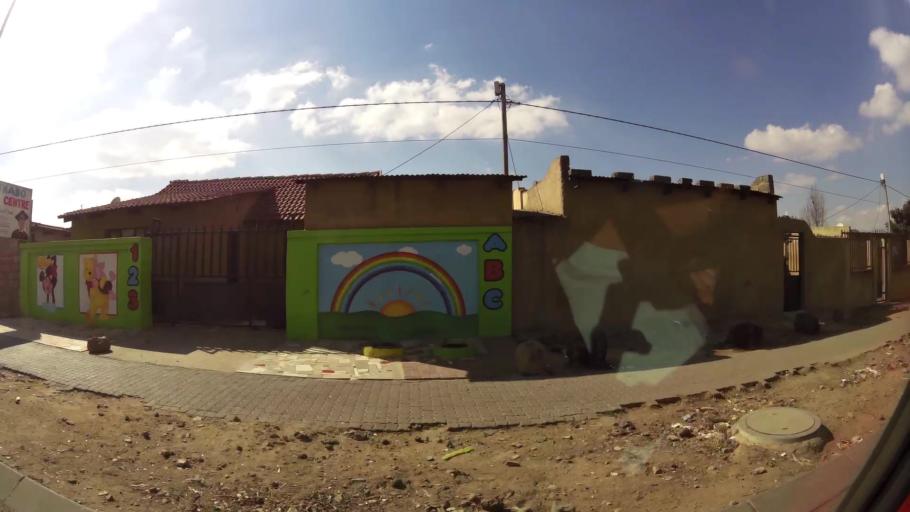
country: ZA
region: Gauteng
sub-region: Ekurhuleni Metropolitan Municipality
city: Tembisa
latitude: -26.0104
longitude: 28.1859
